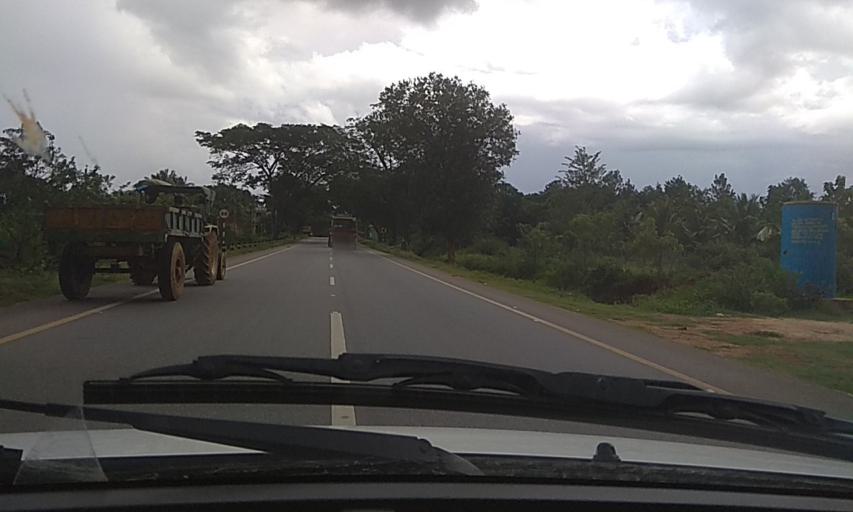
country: IN
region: Karnataka
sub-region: Tumkur
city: Kunigal
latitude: 13.1298
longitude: 77.0289
